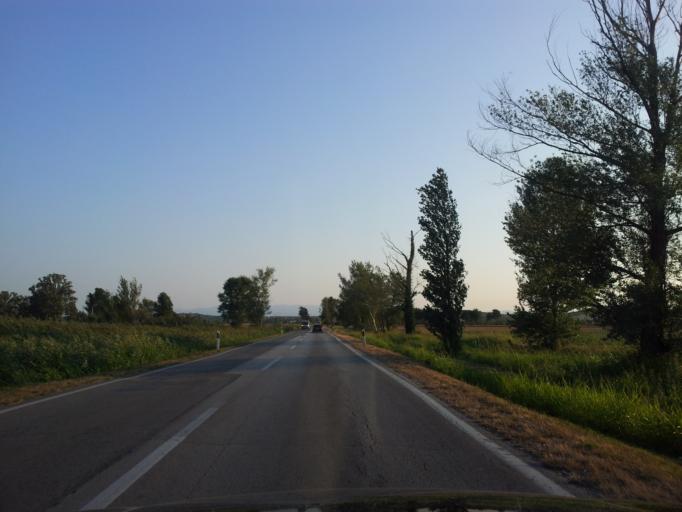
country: HR
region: Zadarska
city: Biograd na Moru
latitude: 43.9723
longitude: 15.4847
